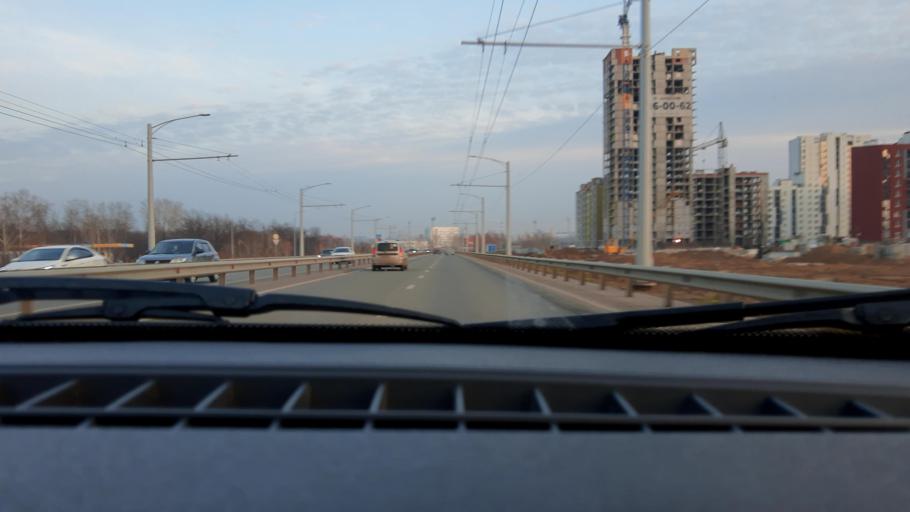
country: RU
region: Bashkortostan
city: Mikhaylovka
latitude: 54.7732
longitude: 55.8993
